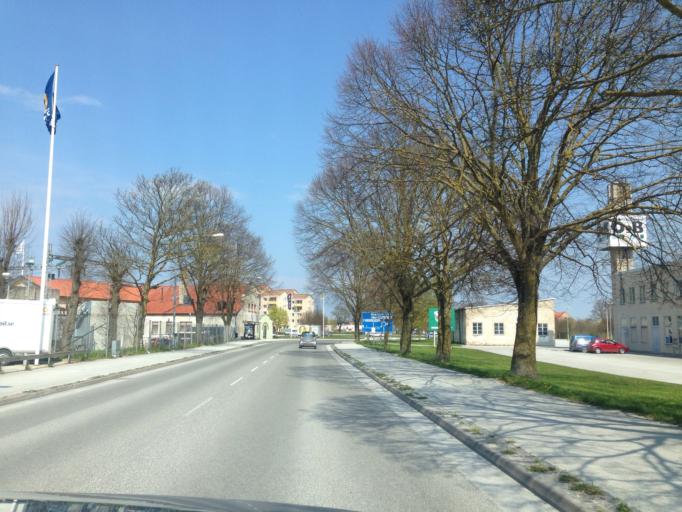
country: SE
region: Gotland
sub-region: Gotland
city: Visby
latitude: 57.6298
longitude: 18.2879
